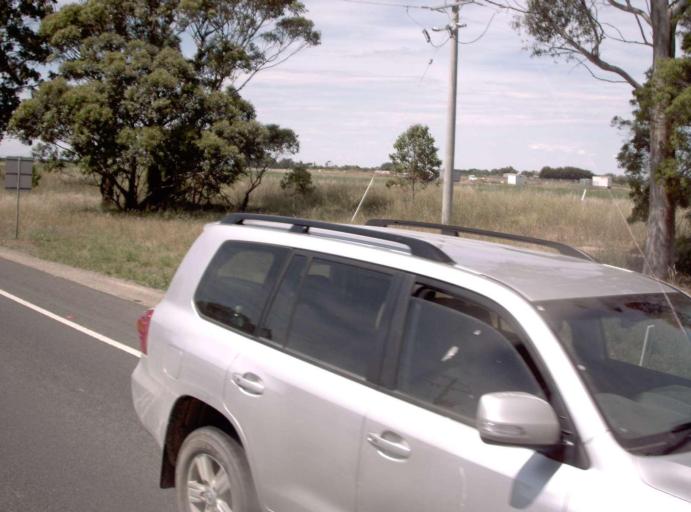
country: AU
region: Victoria
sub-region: Wellington
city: Sale
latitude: -38.0844
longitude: 147.0707
